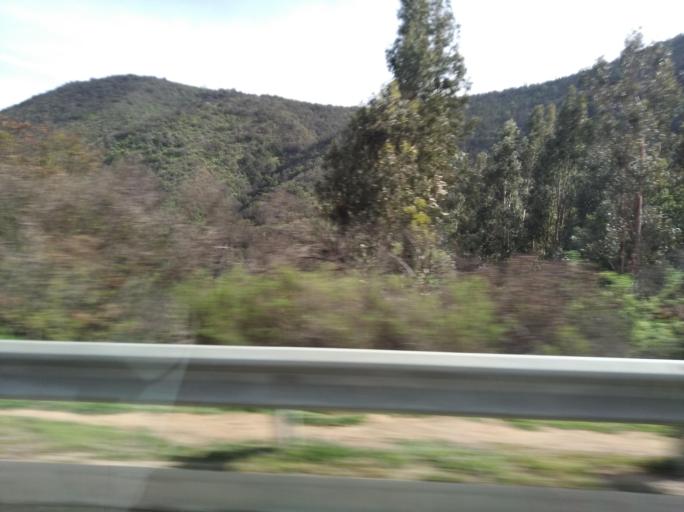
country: CL
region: Valparaiso
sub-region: Provincia de Marga Marga
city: Limache
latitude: -33.0605
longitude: -71.0574
